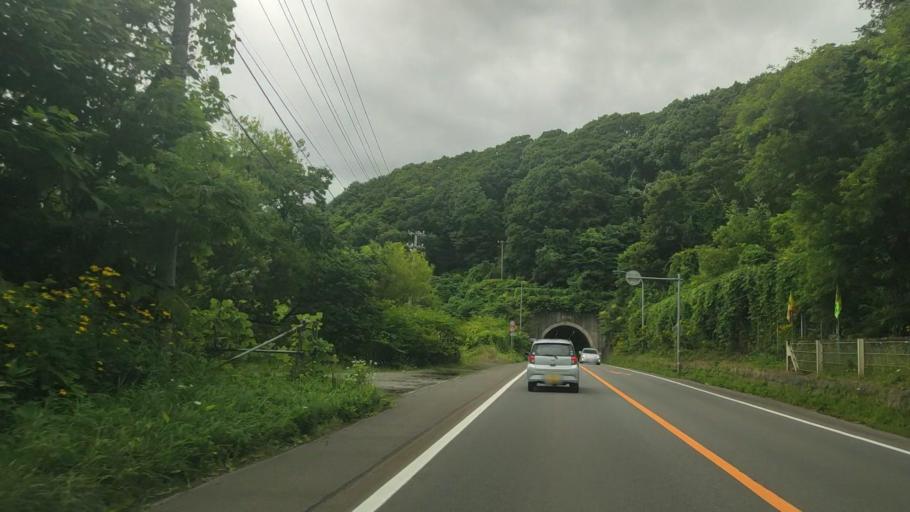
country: JP
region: Hokkaido
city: Date
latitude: 42.5697
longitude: 140.7345
